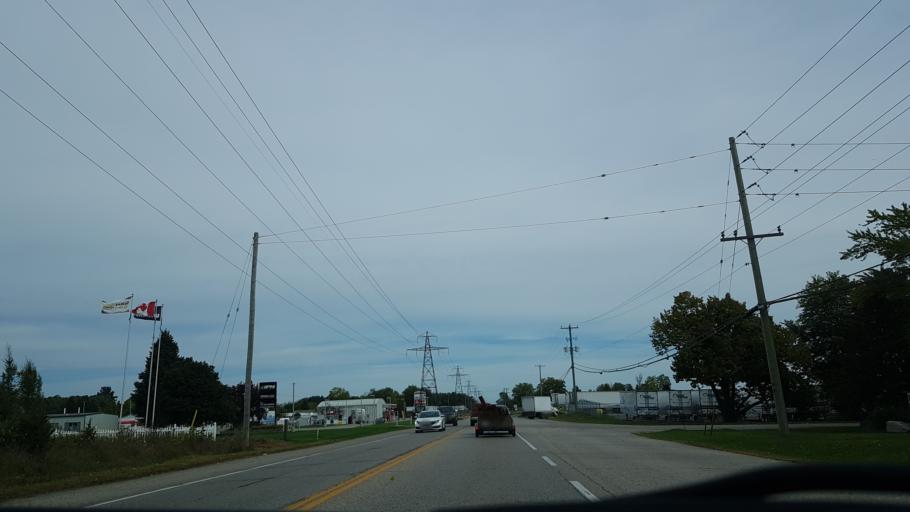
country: CA
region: Ontario
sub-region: Wellington County
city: Guelph
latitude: 43.4940
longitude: -80.2803
